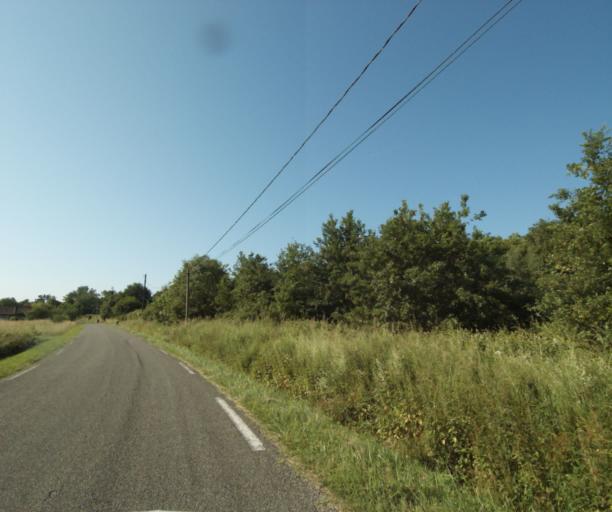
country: FR
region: Midi-Pyrenees
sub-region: Departement du Tarn-et-Garonne
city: Saint-Etienne-de-Tulmont
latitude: 44.0251
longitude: 1.4261
